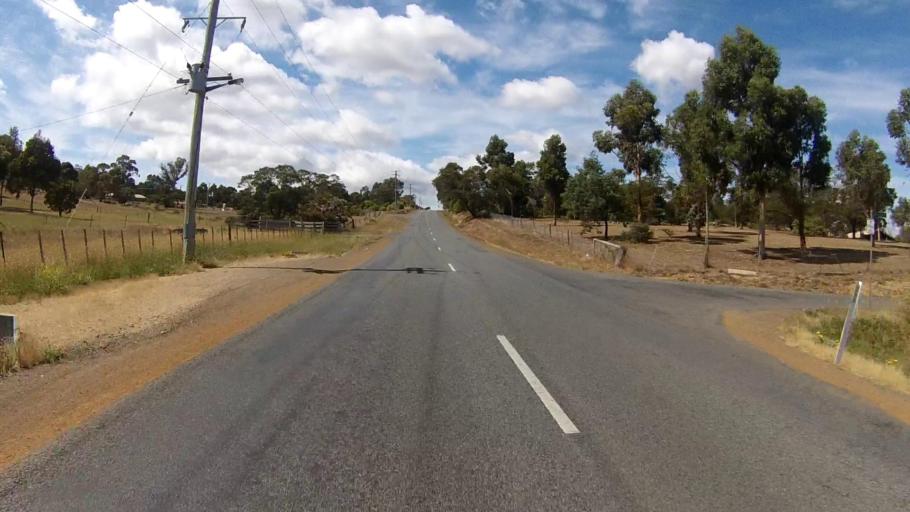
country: AU
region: Tasmania
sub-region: Brighton
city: Bridgewater
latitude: -42.7116
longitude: 147.2709
